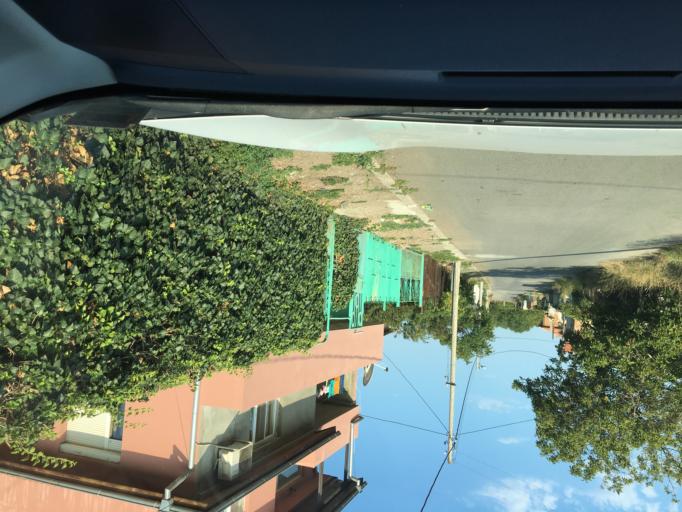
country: BG
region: Burgas
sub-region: Obshtina Burgas
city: Burgas
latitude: 42.6153
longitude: 27.4860
